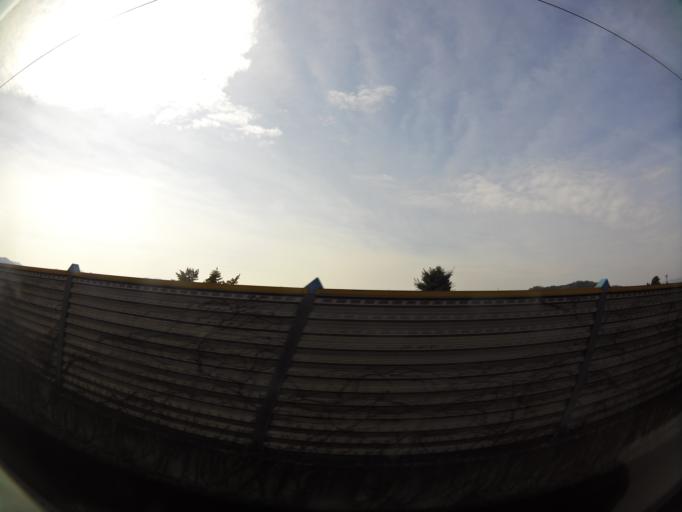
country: KR
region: Daejeon
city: Songgang-dong
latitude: 36.5761
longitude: 127.3115
